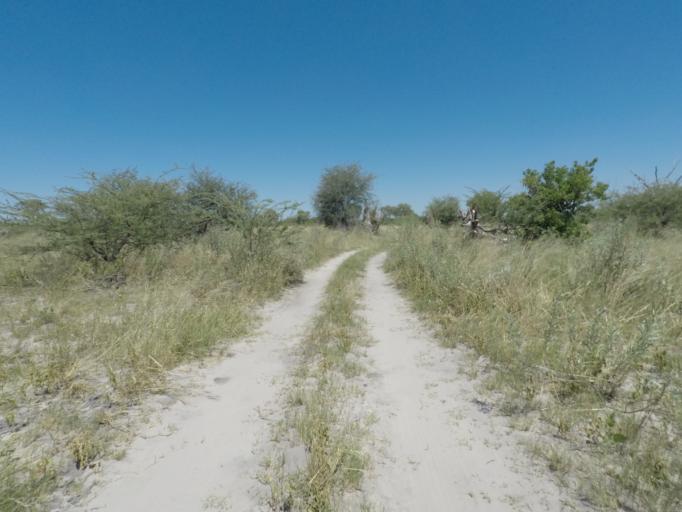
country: BW
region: North West
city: Maun
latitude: -19.4477
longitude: 23.5569
